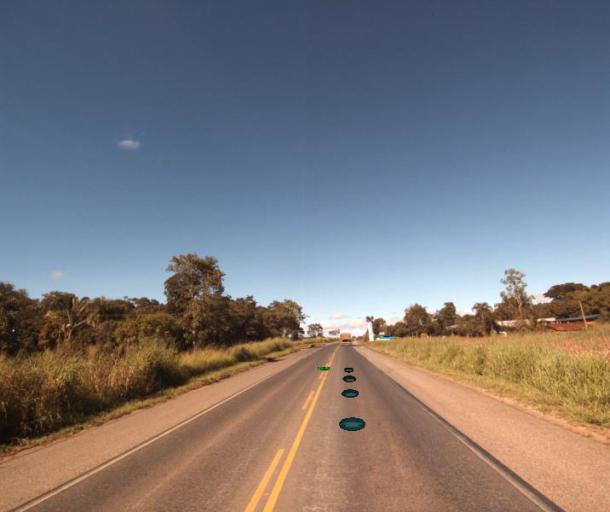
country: BR
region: Goias
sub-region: Itapaci
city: Itapaci
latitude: -15.0224
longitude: -49.4260
